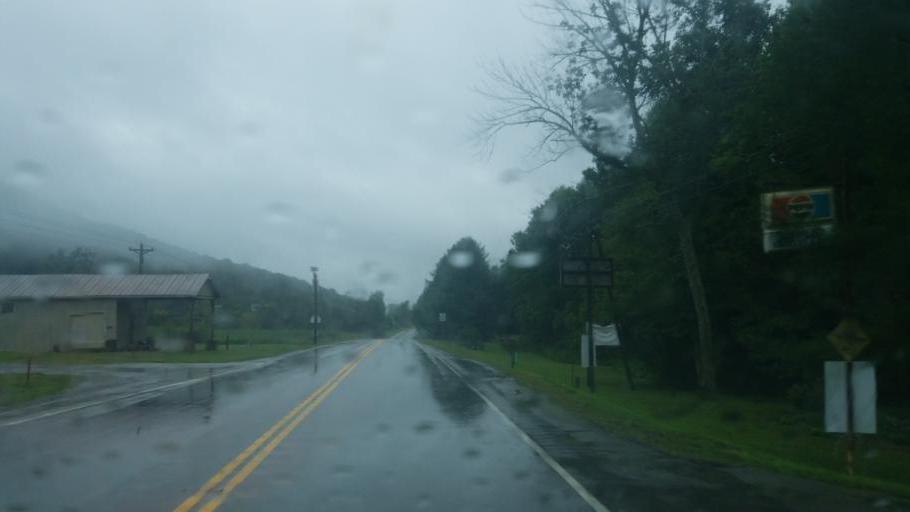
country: US
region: Kentucky
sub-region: Fleming County
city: Flemingsburg
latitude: 38.3341
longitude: -83.5936
